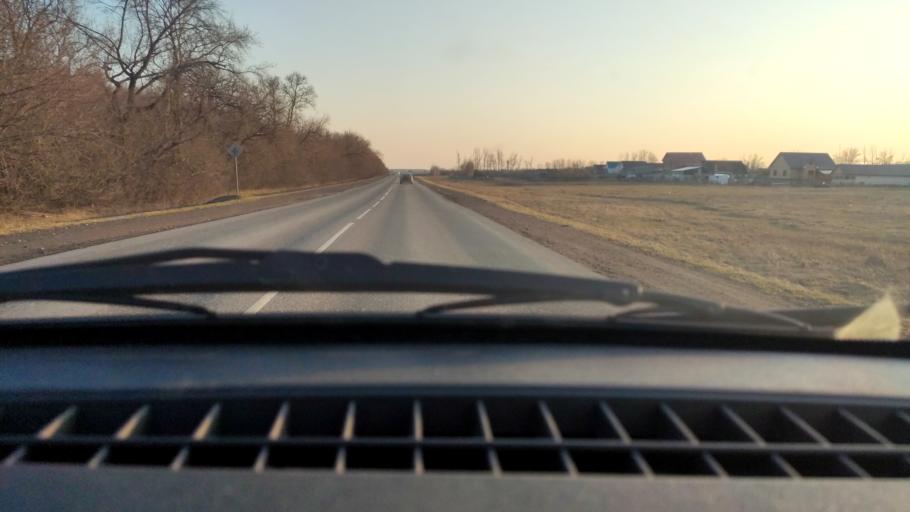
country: RU
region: Bashkortostan
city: Davlekanovo
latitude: 54.2927
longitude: 55.1230
